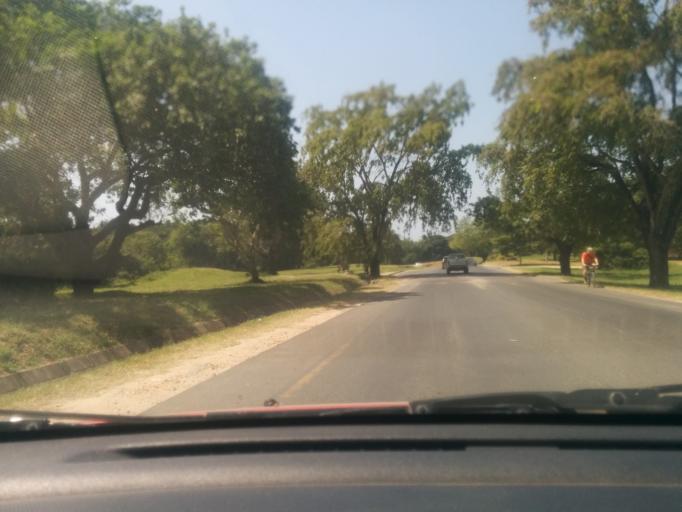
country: TZ
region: Dar es Salaam
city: Magomeni
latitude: -6.7737
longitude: 39.2113
